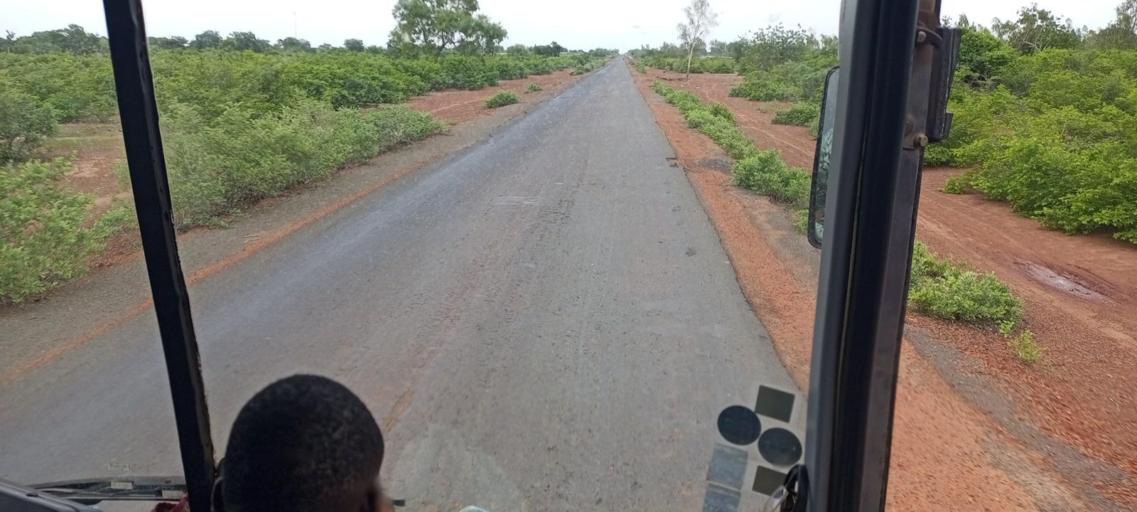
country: ML
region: Sikasso
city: Koutiala
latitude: 12.5436
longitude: -5.5780
